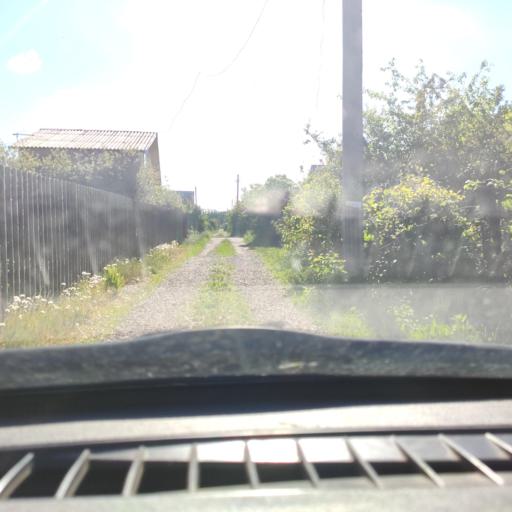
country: RU
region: Samara
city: Tol'yatti
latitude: 53.6271
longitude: 49.4060
